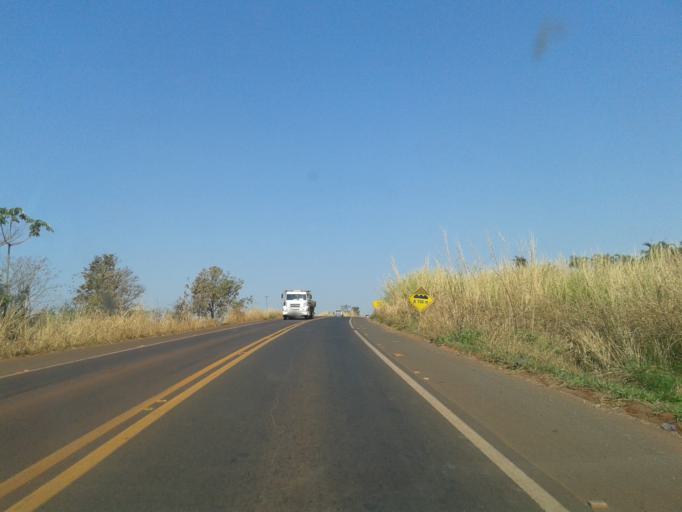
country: BR
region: Minas Gerais
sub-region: Ituiutaba
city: Ituiutaba
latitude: -18.9629
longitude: -49.4756
